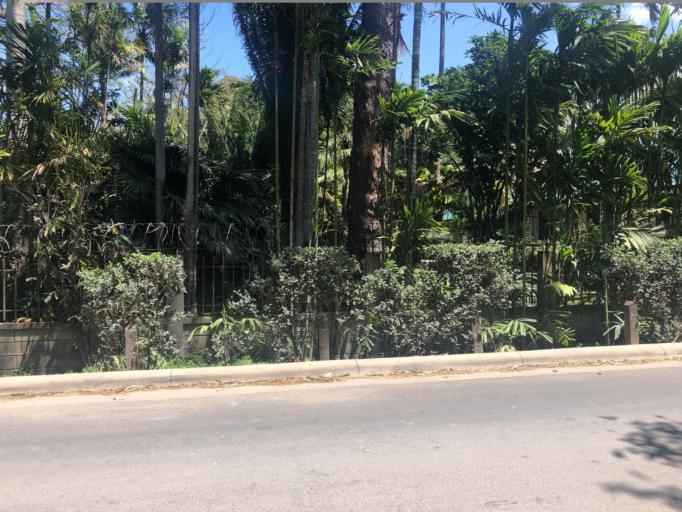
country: CR
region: San Jose
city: Santa Ana
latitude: 9.9354
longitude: -84.1763
